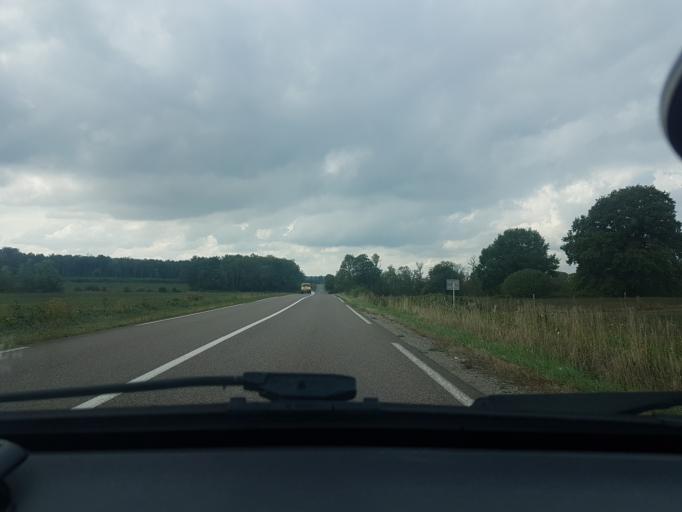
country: FR
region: Franche-Comte
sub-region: Departement de la Haute-Saone
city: Villersexel
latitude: 47.5436
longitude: 6.5051
